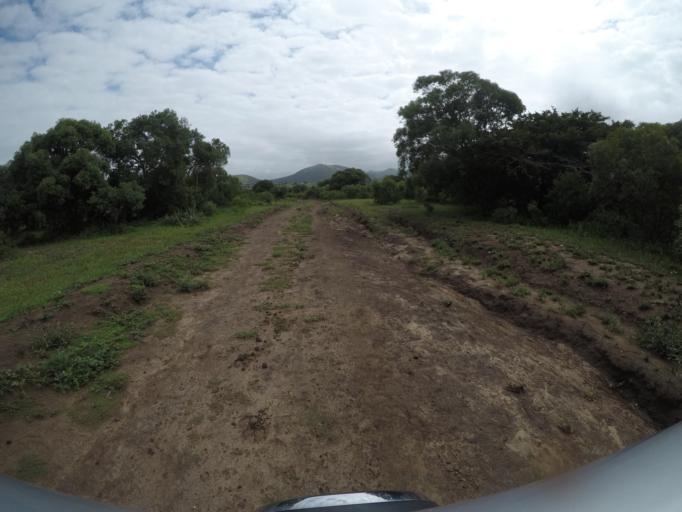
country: ZA
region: KwaZulu-Natal
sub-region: uThungulu District Municipality
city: Empangeni
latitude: -28.6230
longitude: 31.8652
